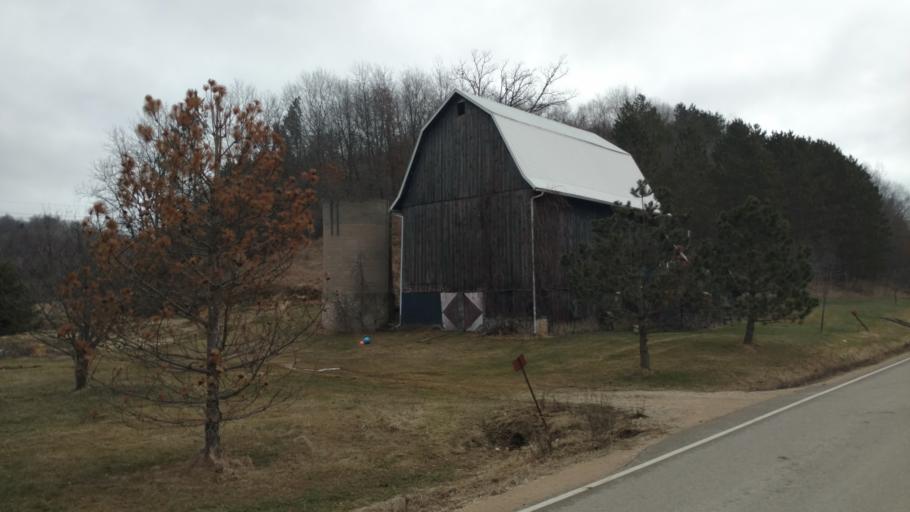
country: US
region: Wisconsin
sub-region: Vernon County
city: Hillsboro
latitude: 43.6460
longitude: -90.4852
